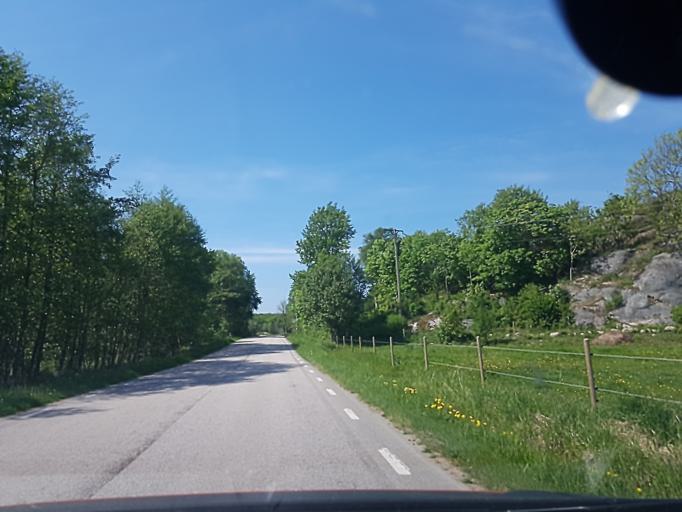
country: SE
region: Vaestra Goetaland
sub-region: Lysekils Kommun
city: Lysekil
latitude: 58.1626
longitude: 11.4521
